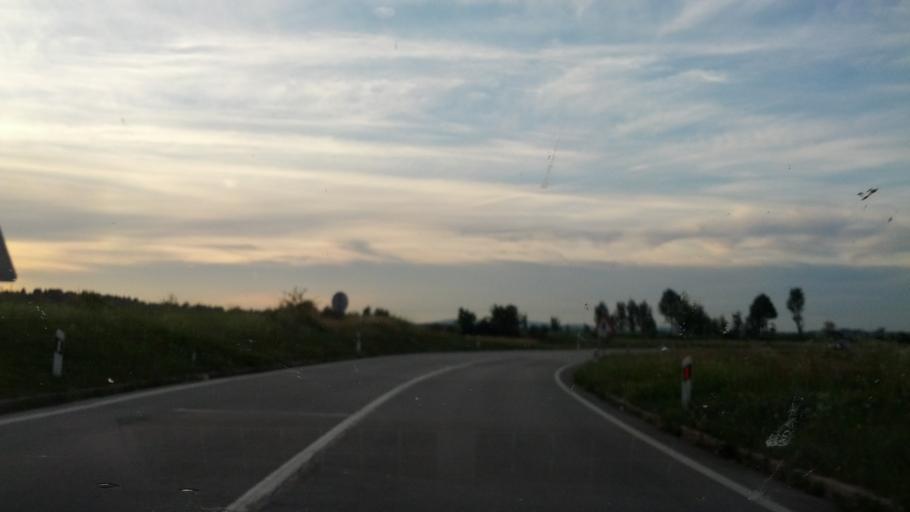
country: BA
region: Federation of Bosnia and Herzegovina
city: Izacic
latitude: 44.8757
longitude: 15.7692
